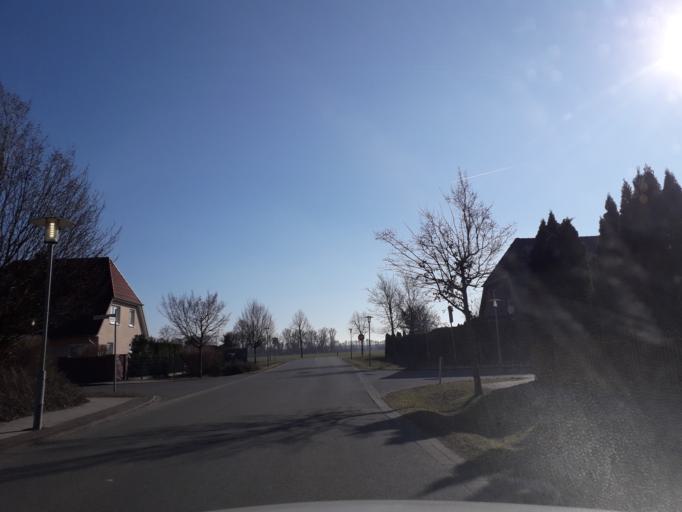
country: DE
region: Brandenburg
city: Brieselang
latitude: 52.5761
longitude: 12.9897
